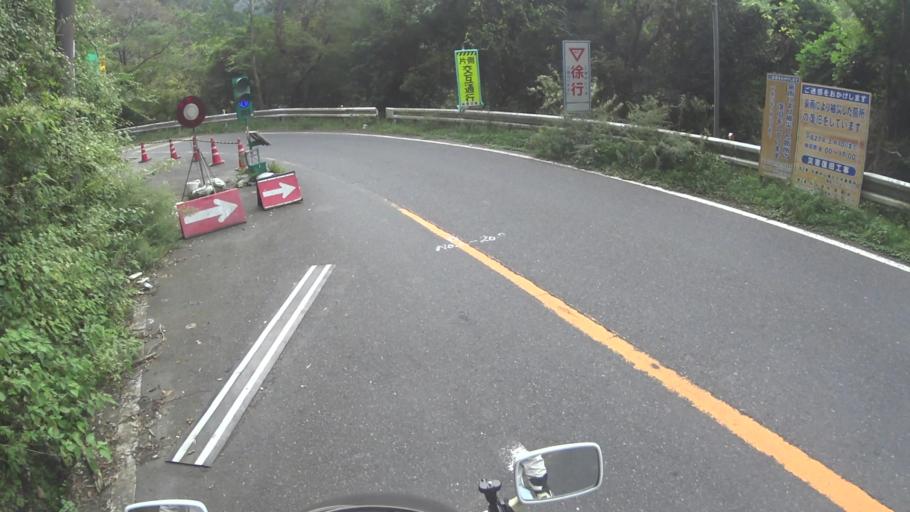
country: JP
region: Kyoto
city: Uji
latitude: 34.8819
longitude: 135.8513
